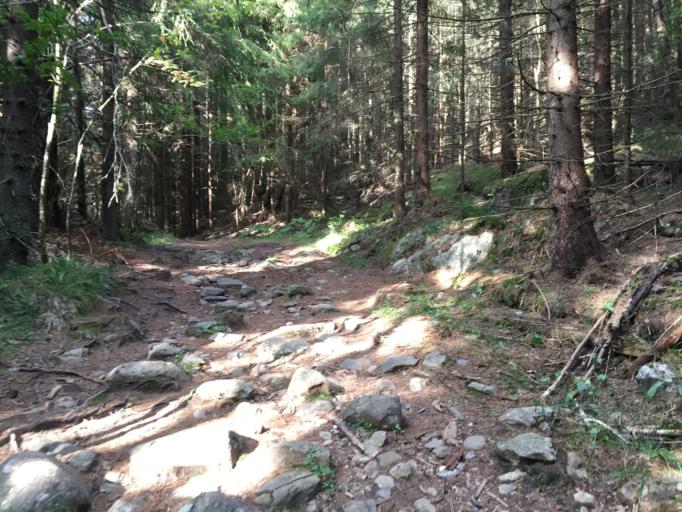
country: NO
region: Akershus
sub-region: Raelingen
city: Fjerdingby
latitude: 59.9124
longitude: 11.0287
